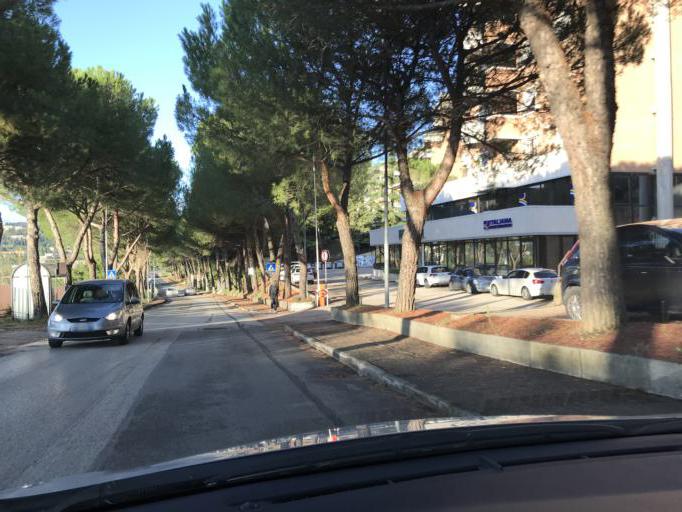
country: IT
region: Umbria
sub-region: Provincia di Perugia
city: Perugia
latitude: 43.1005
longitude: 12.3626
